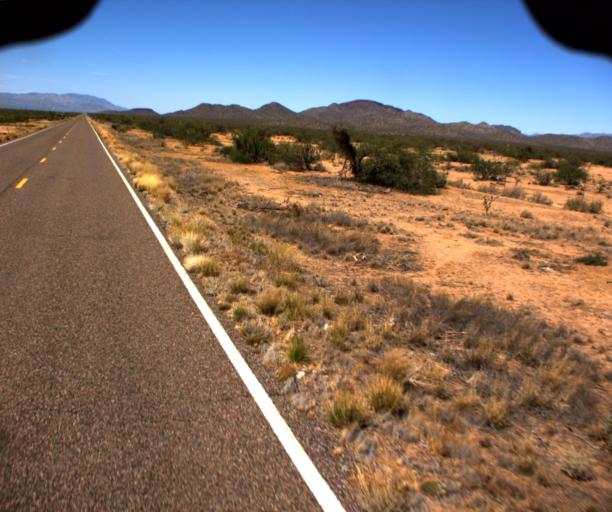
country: US
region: Arizona
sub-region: Yavapai County
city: Congress
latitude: 34.0553
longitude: -113.0523
